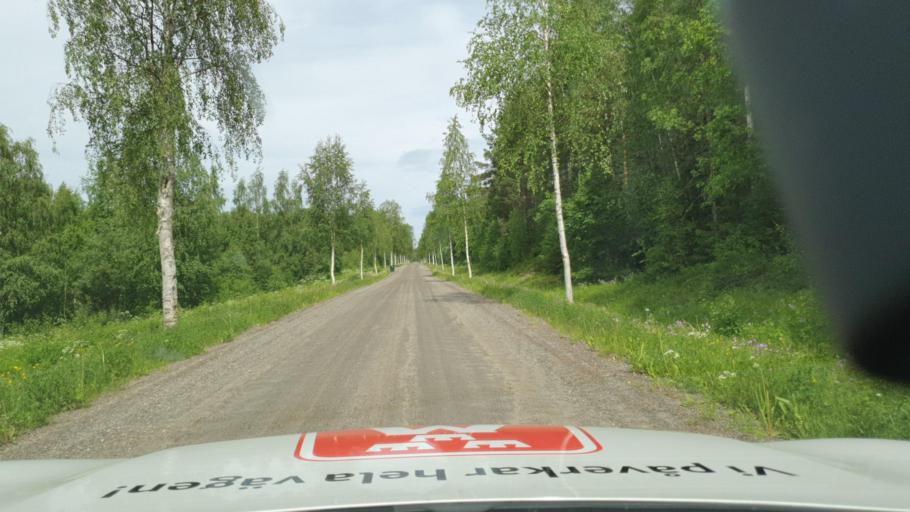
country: SE
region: Vaesterbotten
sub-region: Skelleftea Kommun
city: Burtraesk
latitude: 64.4664
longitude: 20.4686
